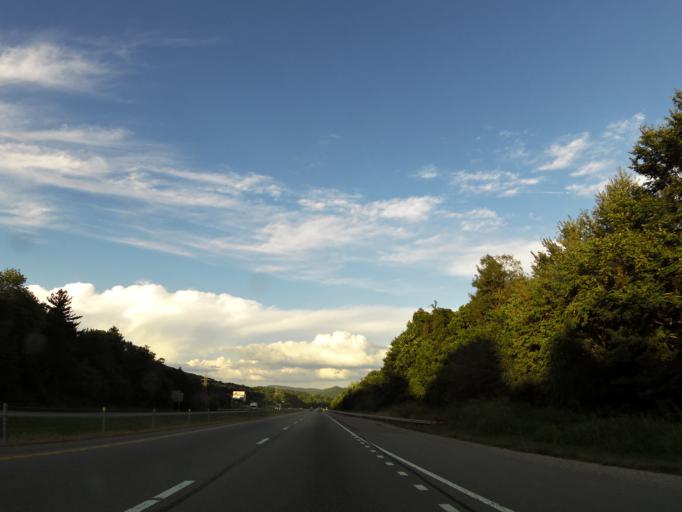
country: US
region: Tennessee
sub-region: Putnam County
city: Algood
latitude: 36.1387
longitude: -85.4460
